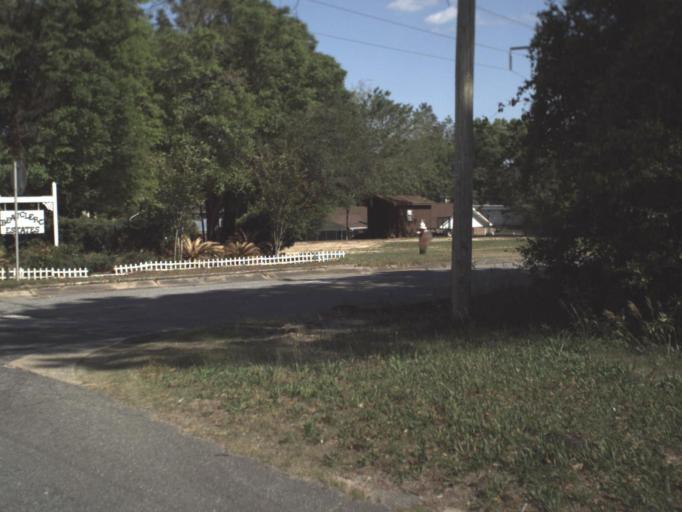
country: US
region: Florida
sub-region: Escambia County
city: Brent
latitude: 30.4963
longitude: -87.2447
